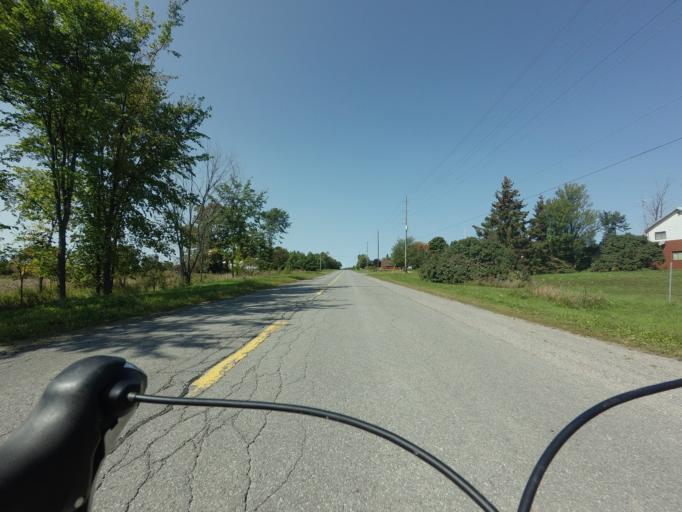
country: CA
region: Ontario
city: Arnprior
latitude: 45.4828
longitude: -76.1257
